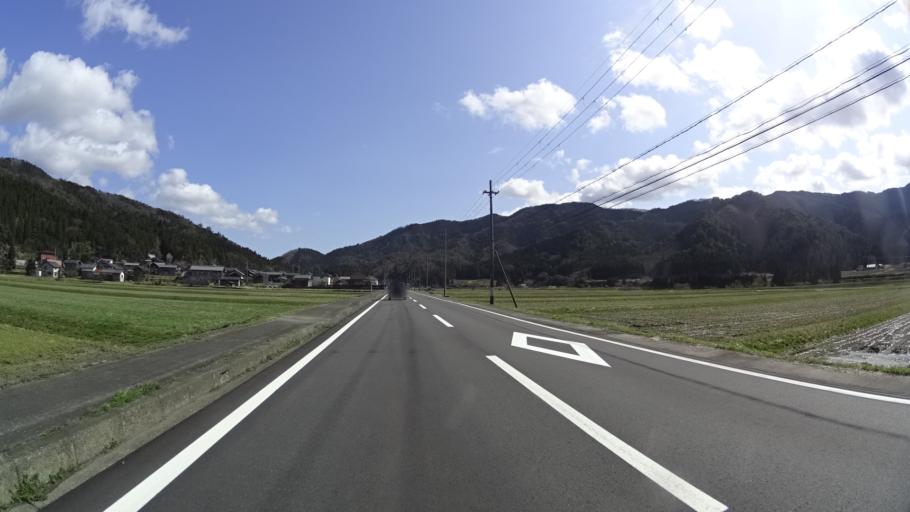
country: JP
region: Fukui
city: Obama
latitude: 35.4560
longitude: 135.8792
